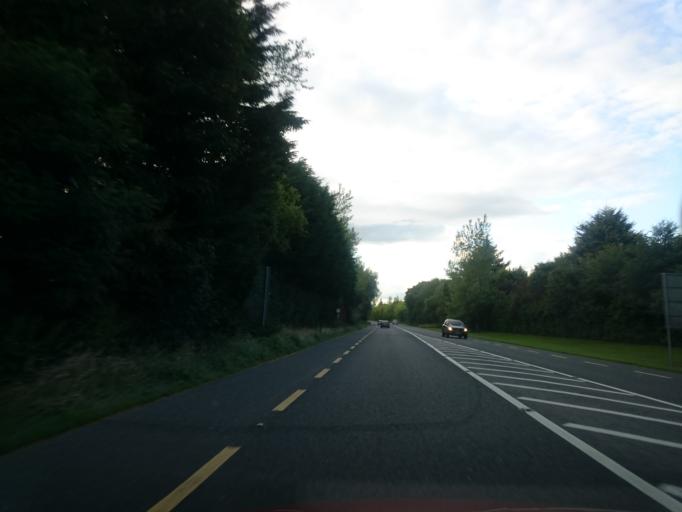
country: IE
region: Leinster
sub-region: Loch Garman
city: Enniscorthy
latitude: 52.4306
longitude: -6.5334
